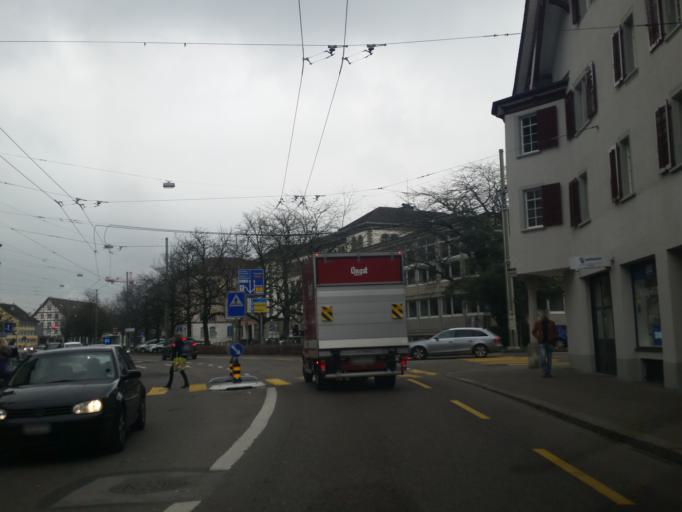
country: CH
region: Zurich
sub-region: Bezirk Winterthur
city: Stadt Winterthur (Kreis 1) / Altstadt
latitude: 47.4978
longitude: 8.7273
